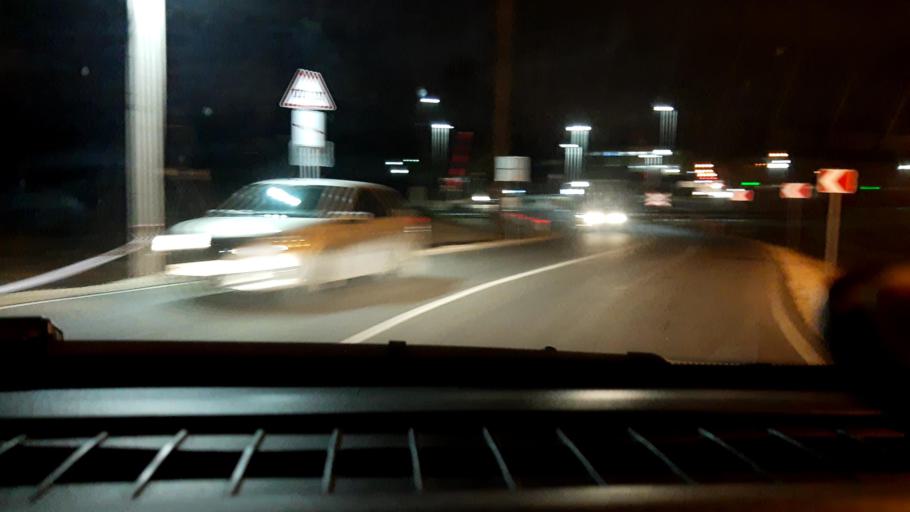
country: RU
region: Nizjnij Novgorod
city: Gorbatovka
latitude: 56.3518
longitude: 43.8391
